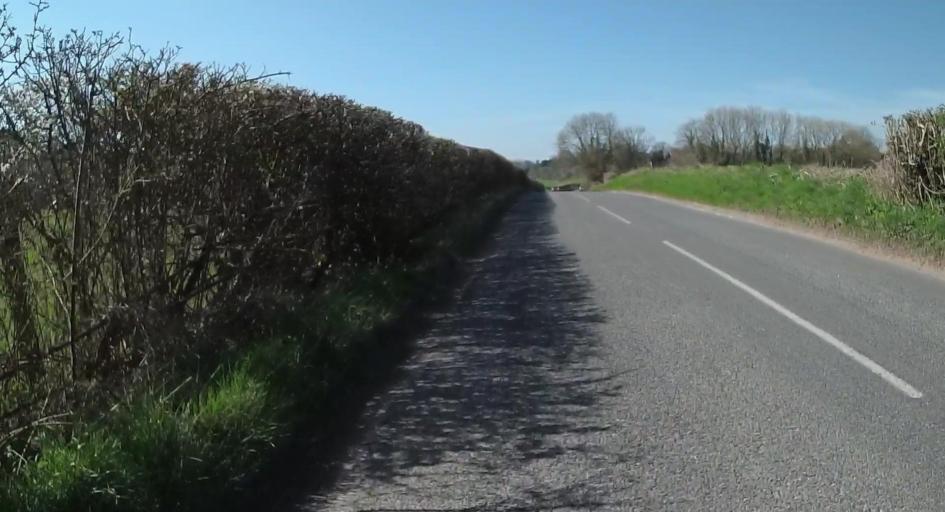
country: GB
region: England
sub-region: Hampshire
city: Andover
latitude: 51.2708
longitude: -1.4383
